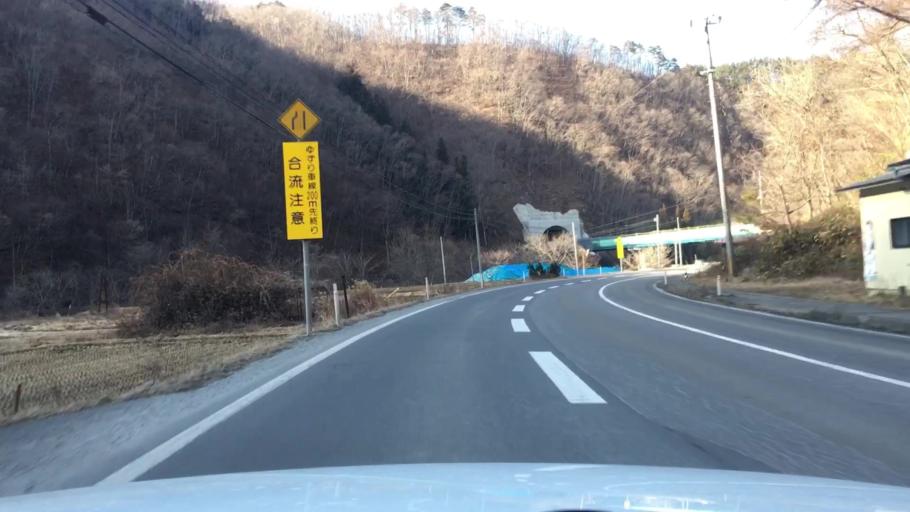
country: JP
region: Iwate
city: Miyako
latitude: 39.5978
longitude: 141.6482
